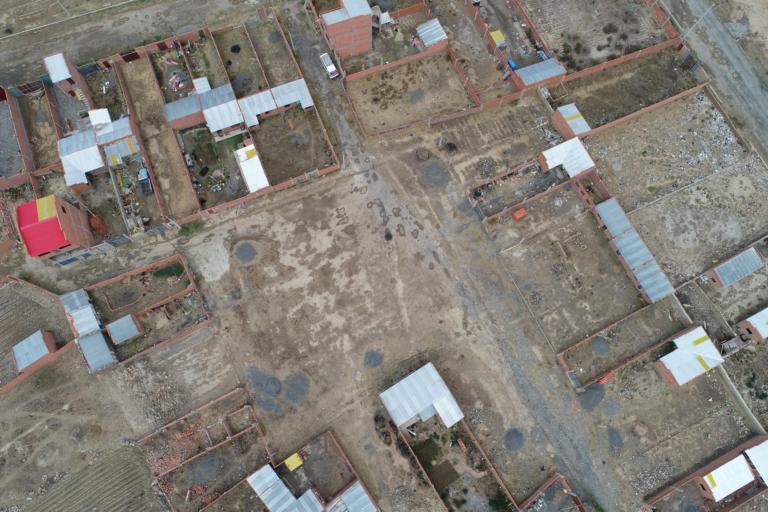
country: BO
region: La Paz
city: Achacachi
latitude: -16.0525
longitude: -68.6780
